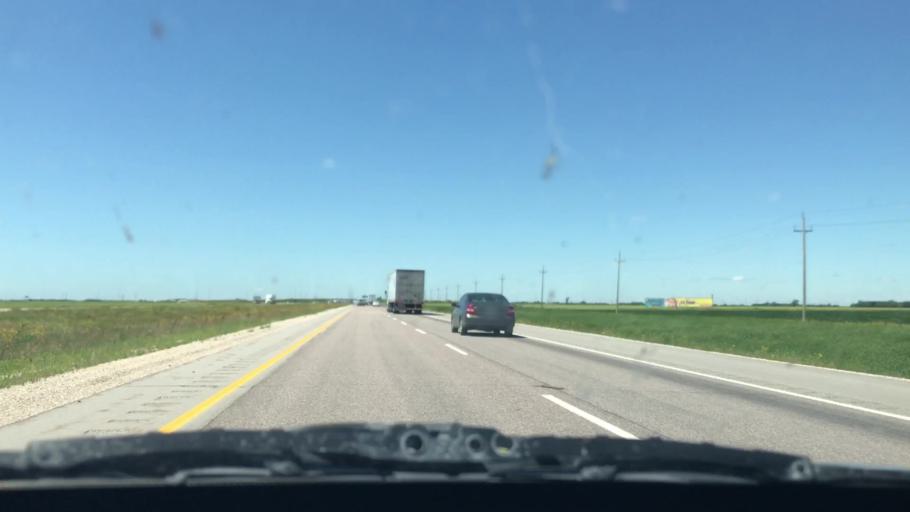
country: CA
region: Manitoba
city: Steinbach
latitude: 49.6923
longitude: -96.6237
